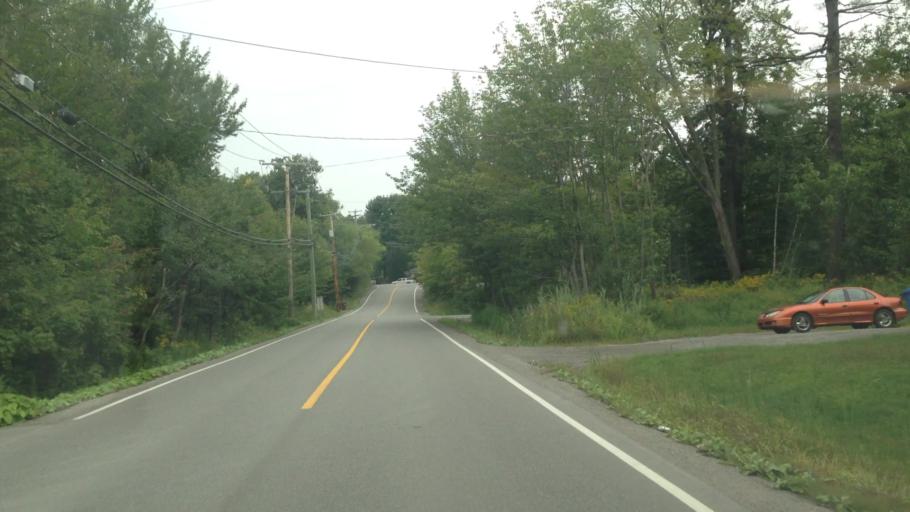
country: CA
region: Quebec
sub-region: Laurentides
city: Saint-Jerome
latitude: 45.8240
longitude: -73.9768
